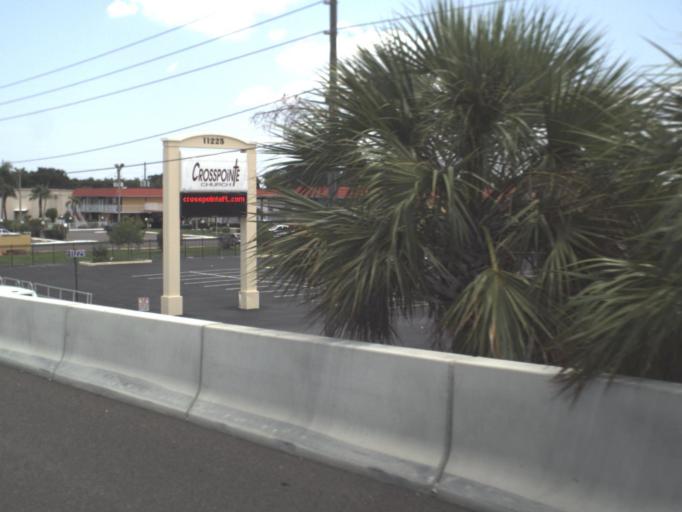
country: US
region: Florida
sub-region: Pinellas County
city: Pinellas Park
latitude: 27.8740
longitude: -82.7083
